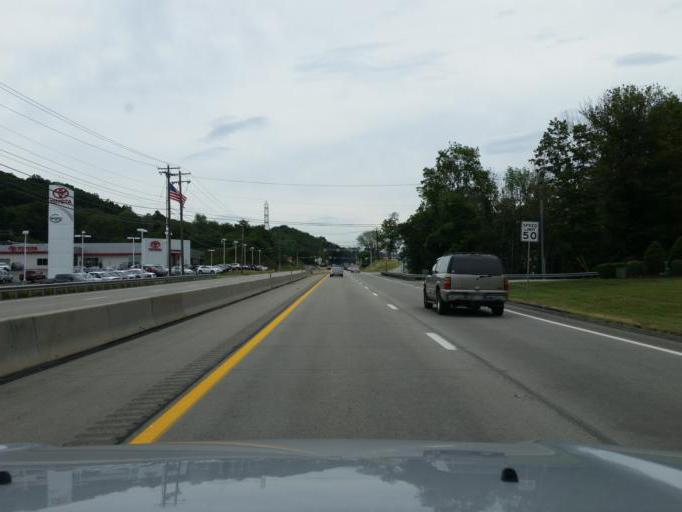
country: US
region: Pennsylvania
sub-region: Westmoreland County
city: Greensburg
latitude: 40.2984
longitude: -79.4832
